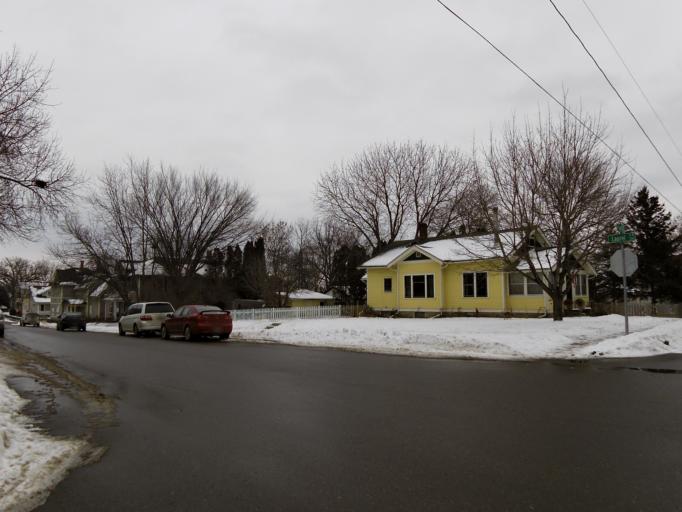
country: US
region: Minnesota
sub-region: Washington County
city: Stillwater
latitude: 45.0604
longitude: -92.8121
